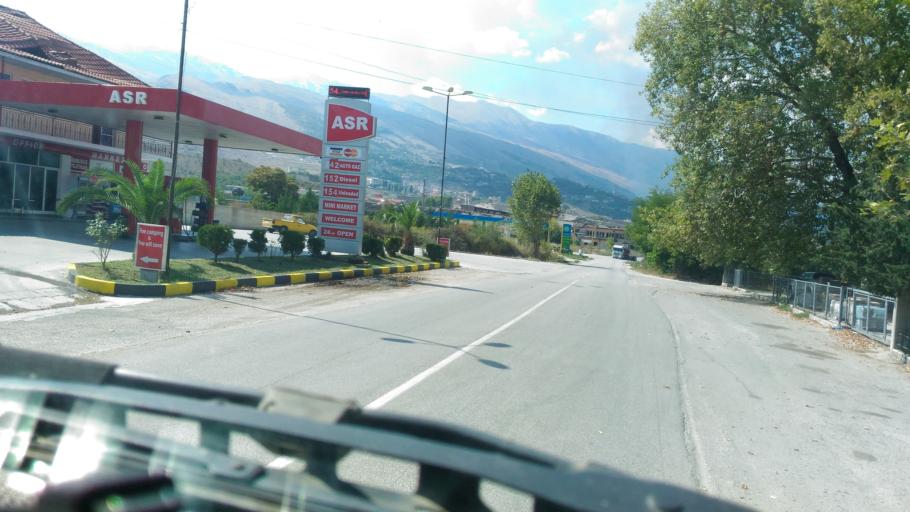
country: AL
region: Gjirokaster
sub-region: Rrethi i Gjirokastres
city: Lazarat
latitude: 40.0647
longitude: 20.1674
